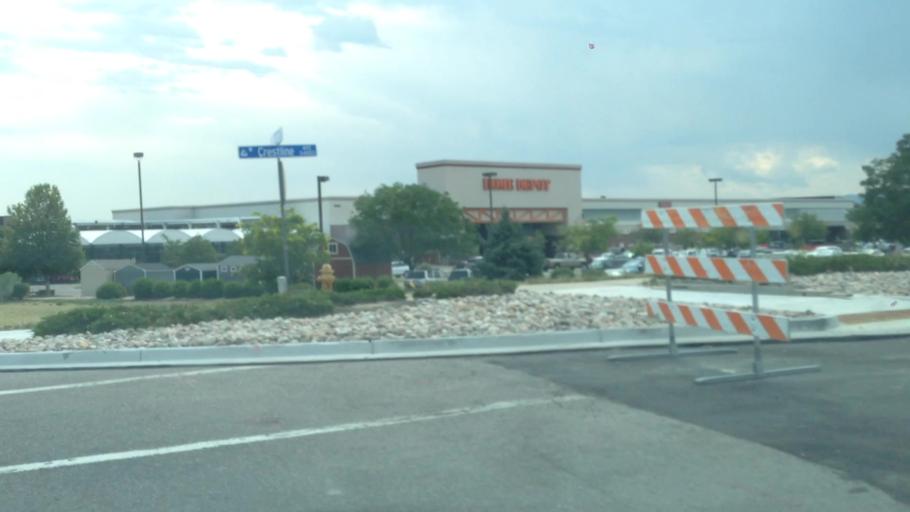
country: US
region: Colorado
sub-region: Jefferson County
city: Columbine
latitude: 39.6189
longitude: -105.0863
